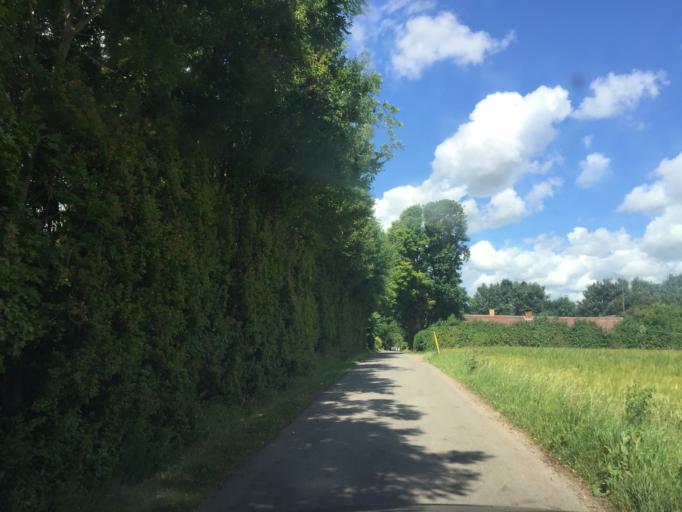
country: DK
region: Capital Region
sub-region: Egedal Kommune
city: Smorumnedre
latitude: 55.7016
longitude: 12.2698
